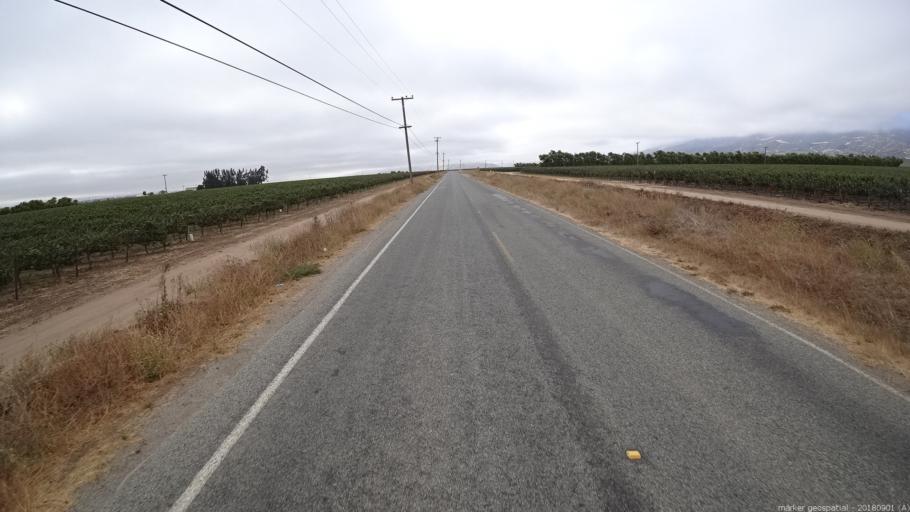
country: US
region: California
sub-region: Monterey County
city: Soledad
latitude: 36.3627
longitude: -121.3216
